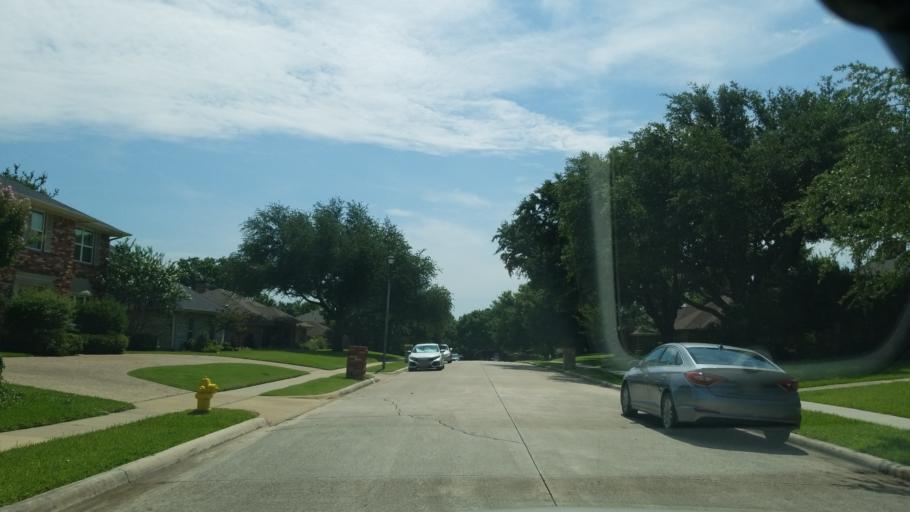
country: US
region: Texas
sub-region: Dallas County
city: Coppell
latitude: 32.9662
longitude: -96.9721
